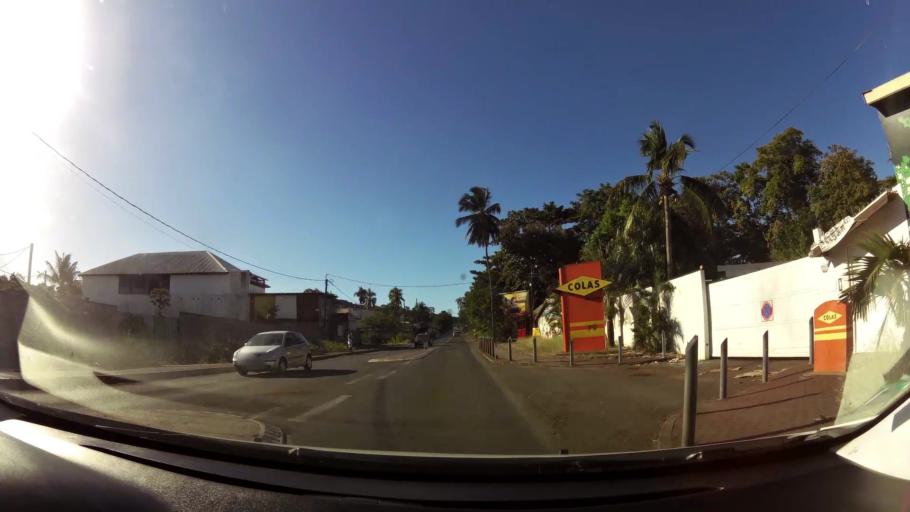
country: YT
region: Mamoudzou
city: Mamoudzou
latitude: -12.7668
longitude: 45.2248
